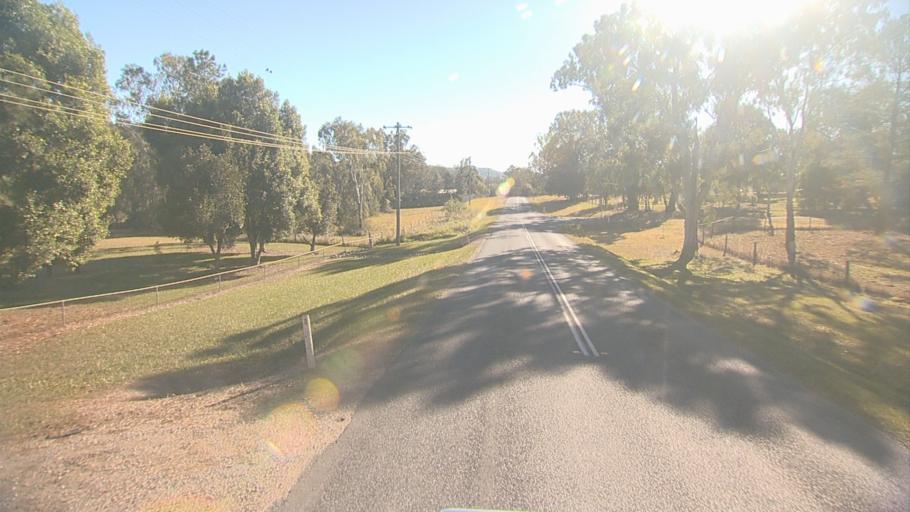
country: AU
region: Queensland
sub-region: Logan
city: Windaroo
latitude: -27.8118
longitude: 153.1704
